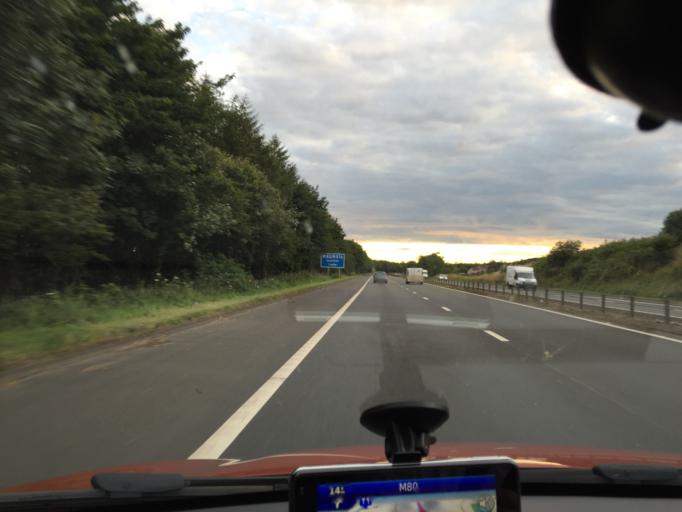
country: GB
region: Scotland
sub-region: Falkirk
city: Bonnybridge
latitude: 56.0047
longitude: -3.8985
